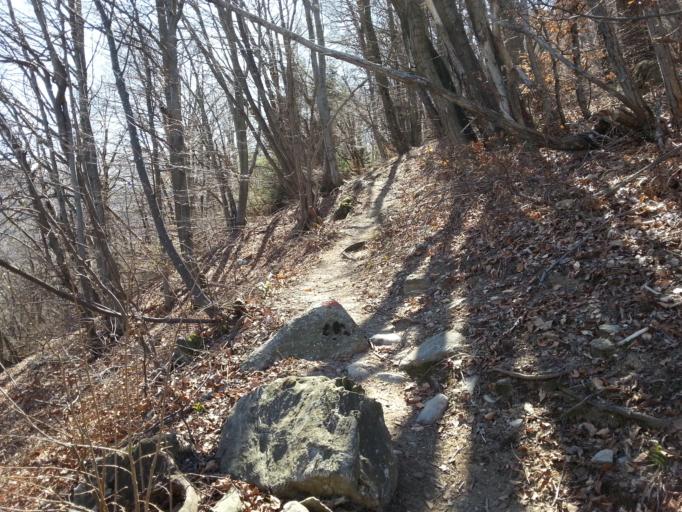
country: IT
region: Lombardy
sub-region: Provincia di Como
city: Magreglio
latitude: 45.9424
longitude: 9.2292
